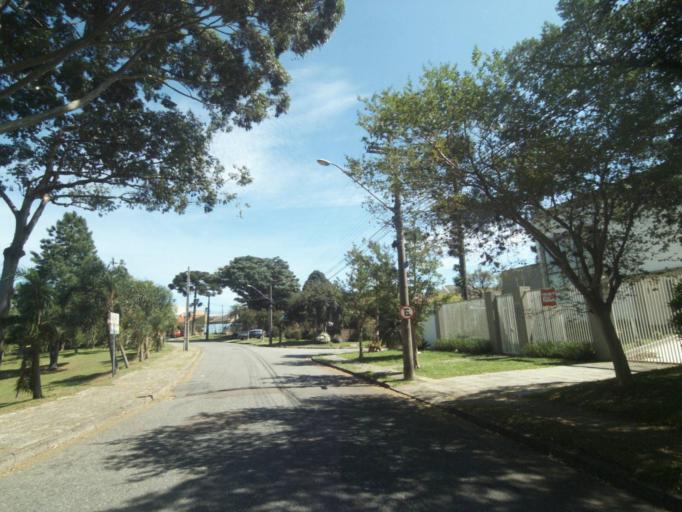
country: BR
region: Parana
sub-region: Curitiba
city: Curitiba
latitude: -25.4572
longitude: -49.2458
